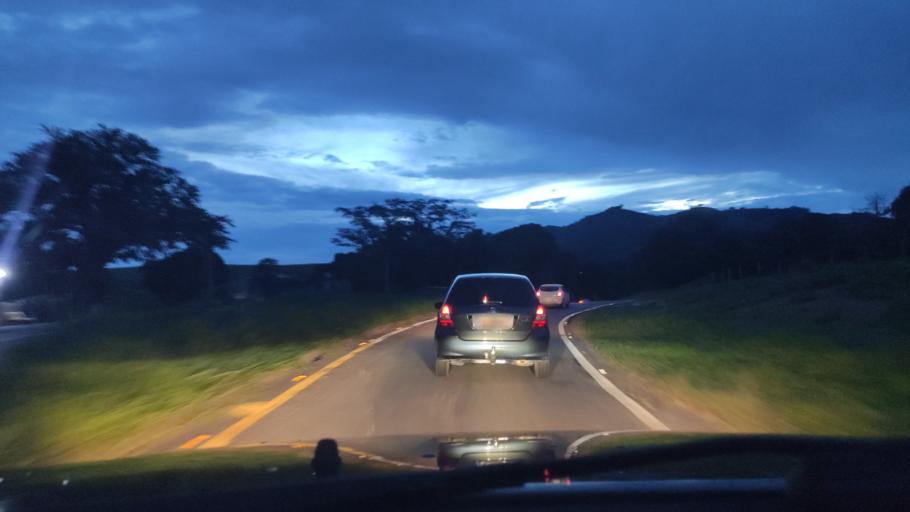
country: BR
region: Sao Paulo
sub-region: Socorro
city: Socorro
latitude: -22.5596
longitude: -46.5549
